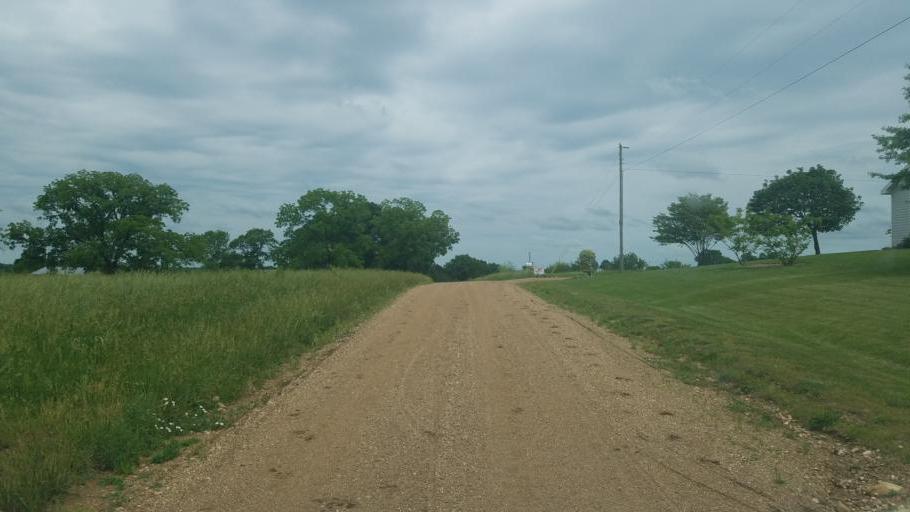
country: US
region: Missouri
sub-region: Moniteau County
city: Tipton
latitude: 38.5515
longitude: -92.7342
